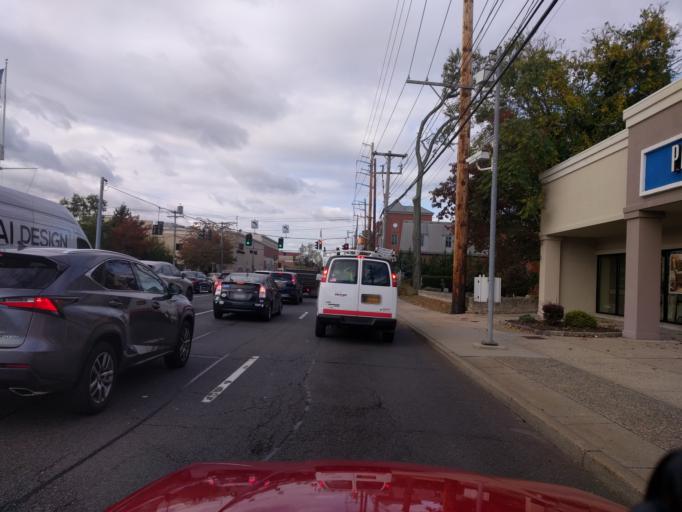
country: US
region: New York
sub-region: Nassau County
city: Manhasset
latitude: 40.7935
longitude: -73.6934
